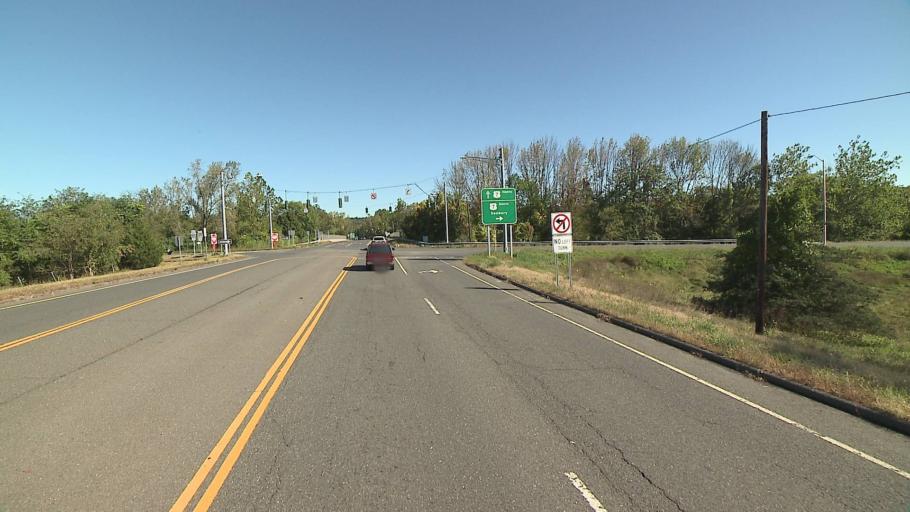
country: US
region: Connecticut
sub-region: Fairfield County
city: Danbury
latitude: 41.4709
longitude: -73.4091
